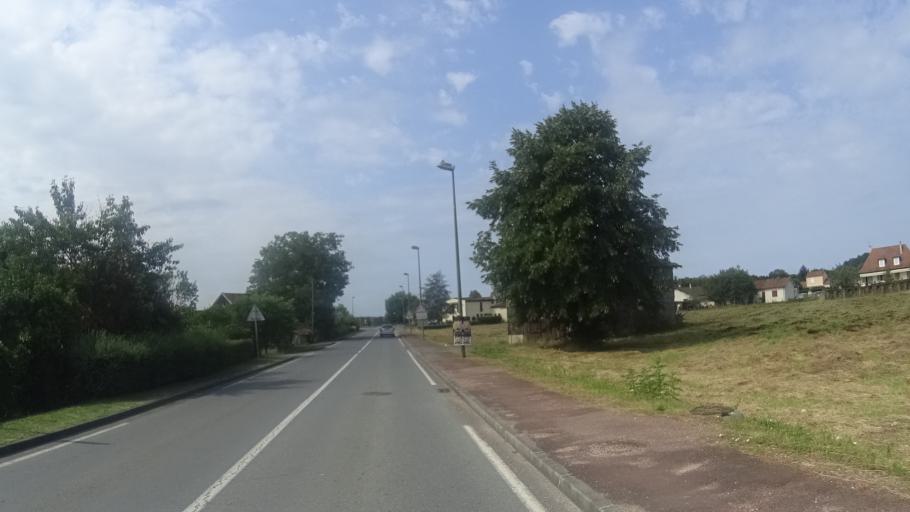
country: FR
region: Aquitaine
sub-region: Departement de la Dordogne
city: Mussidan
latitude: 45.0555
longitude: 0.3641
